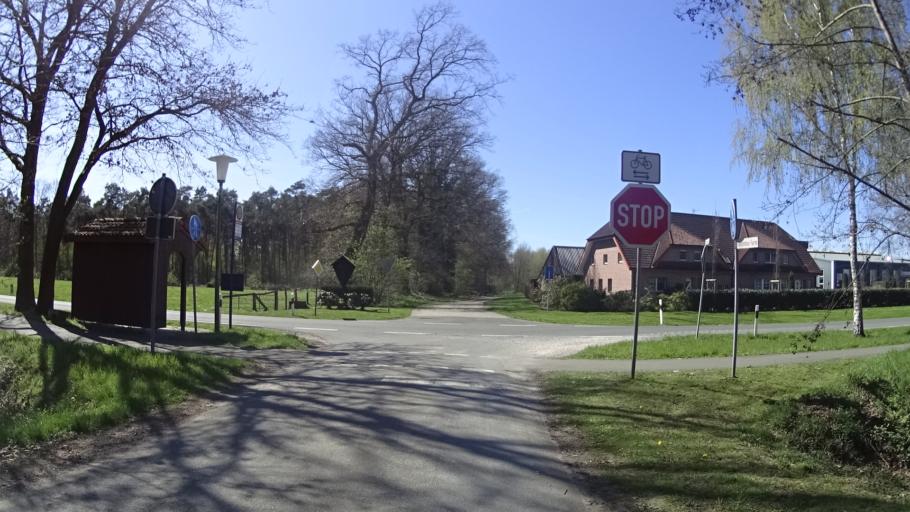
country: DE
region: North Rhine-Westphalia
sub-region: Regierungsbezirk Munster
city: Dulmen
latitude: 51.7896
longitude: 7.2713
